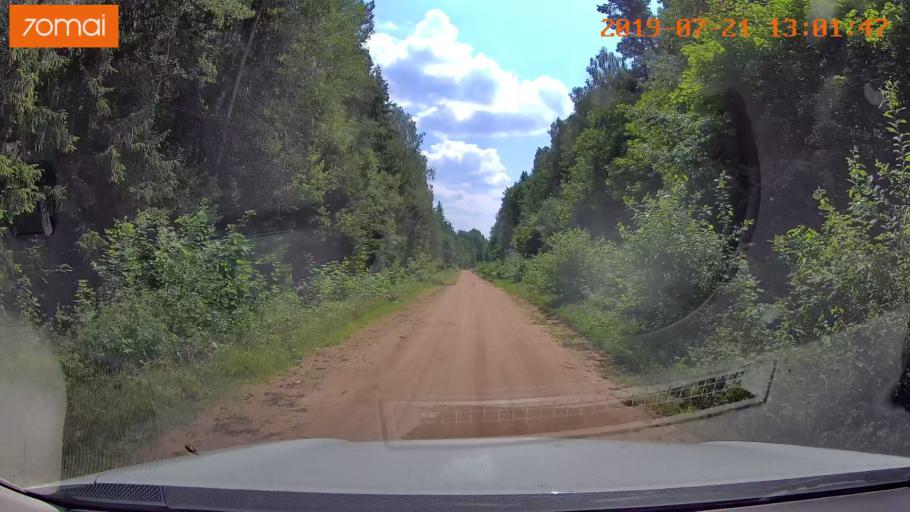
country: BY
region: Grodnenskaya
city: Lyubcha
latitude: 53.8510
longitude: 26.0221
